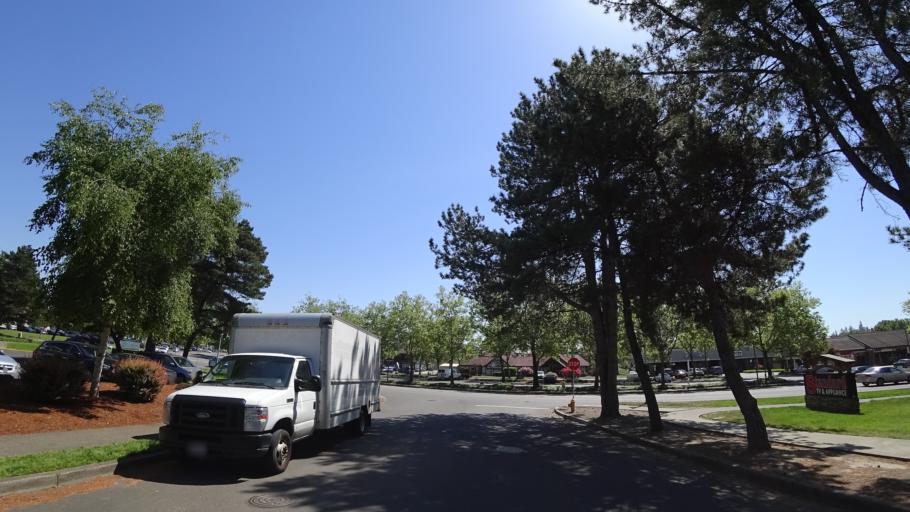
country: US
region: Oregon
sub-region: Washington County
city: Beaverton
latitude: 45.4940
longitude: -122.8078
